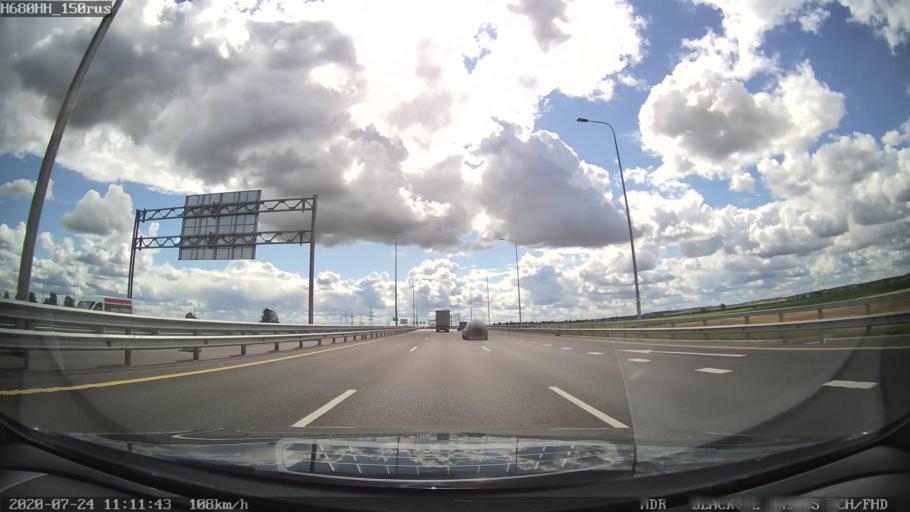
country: RU
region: Leningrad
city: Fedorovskoye
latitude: 59.7187
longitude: 30.5205
